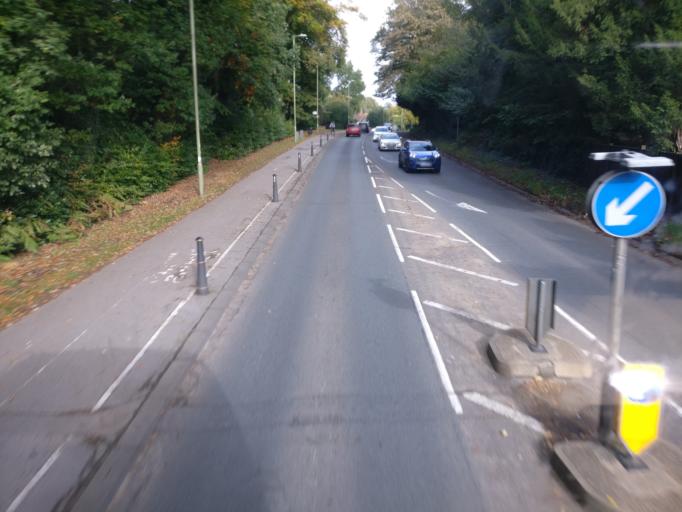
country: GB
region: England
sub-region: Hampshire
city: Farnborough
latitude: 51.2990
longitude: -0.7532
